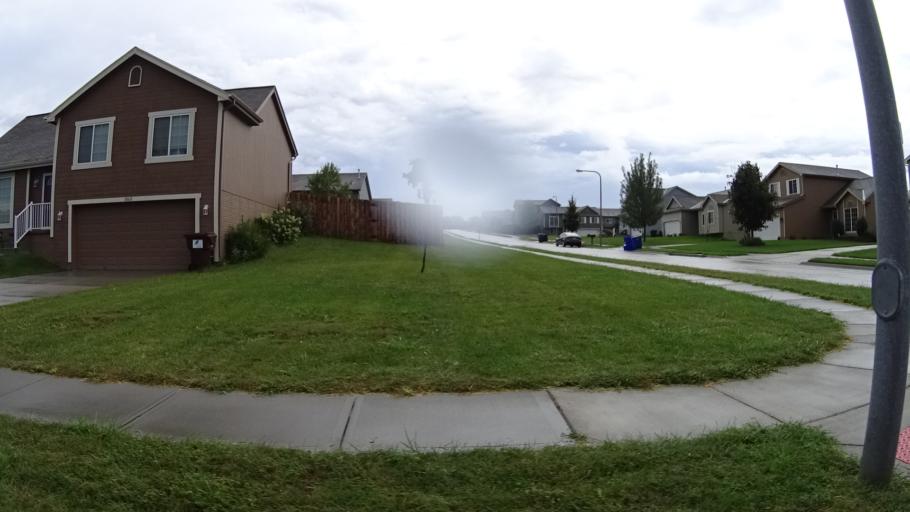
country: US
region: Nebraska
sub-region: Sarpy County
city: Offutt Air Force Base
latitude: 41.1551
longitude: -95.9518
